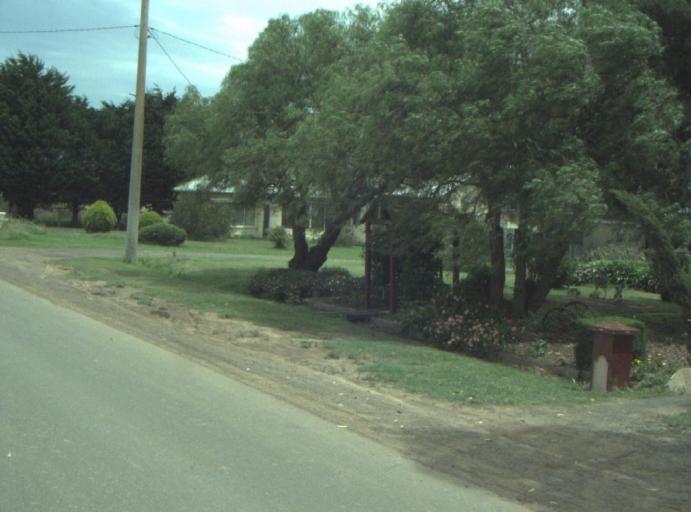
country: AU
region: Victoria
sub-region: Greater Geelong
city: Leopold
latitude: -38.1981
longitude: 144.4533
